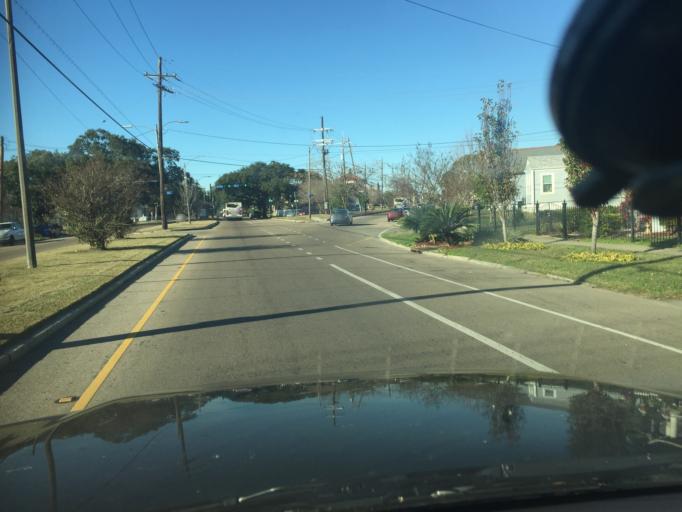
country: US
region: Louisiana
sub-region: Orleans Parish
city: New Orleans
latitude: 29.9846
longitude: -90.0724
